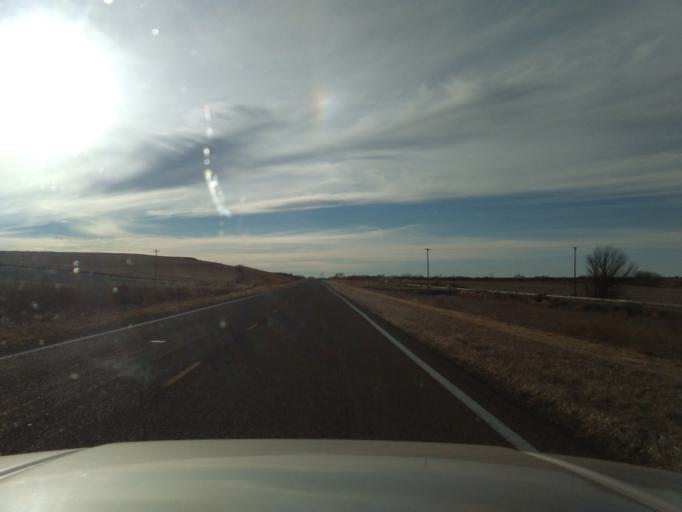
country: US
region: Kansas
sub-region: Norton County
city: Norton
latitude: 39.7483
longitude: -100.1505
